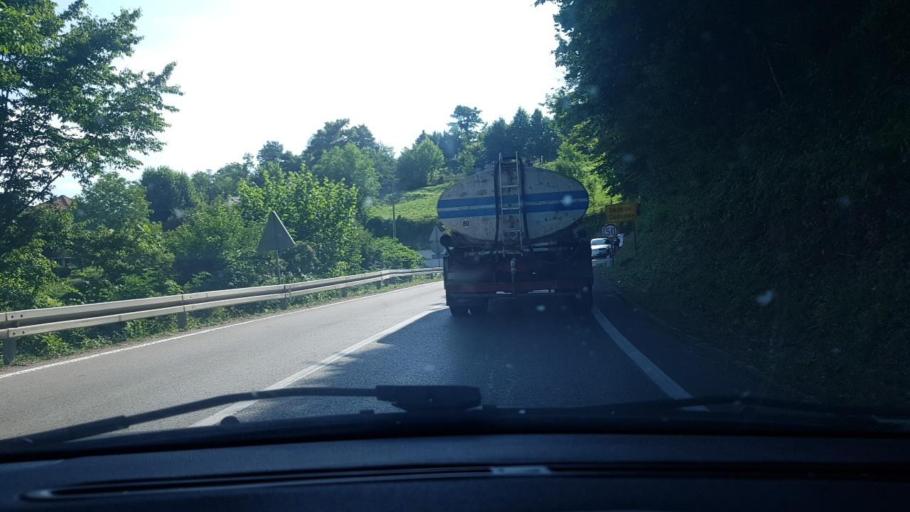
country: BA
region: Federation of Bosnia and Herzegovina
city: Skokovi
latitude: 45.0298
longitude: 15.9129
